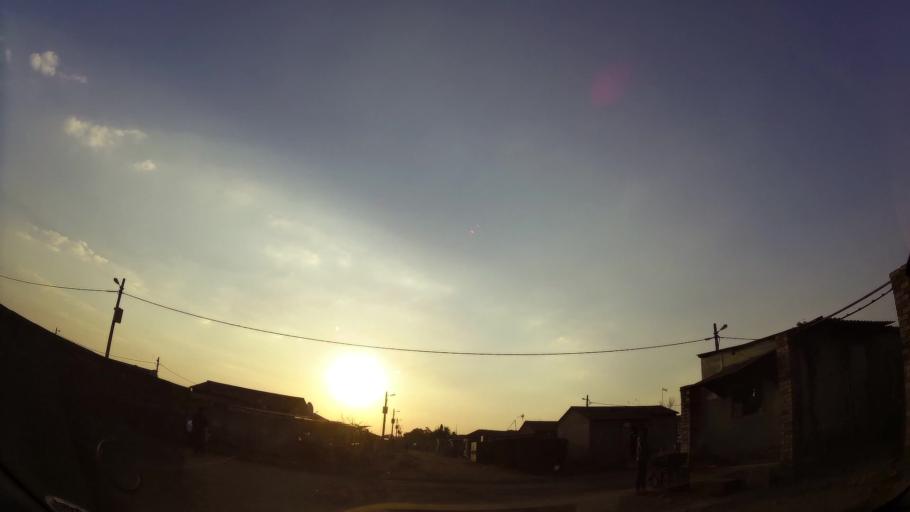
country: ZA
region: Gauteng
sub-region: Ekurhuleni Metropolitan Municipality
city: Benoni
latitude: -26.1616
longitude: 28.3751
